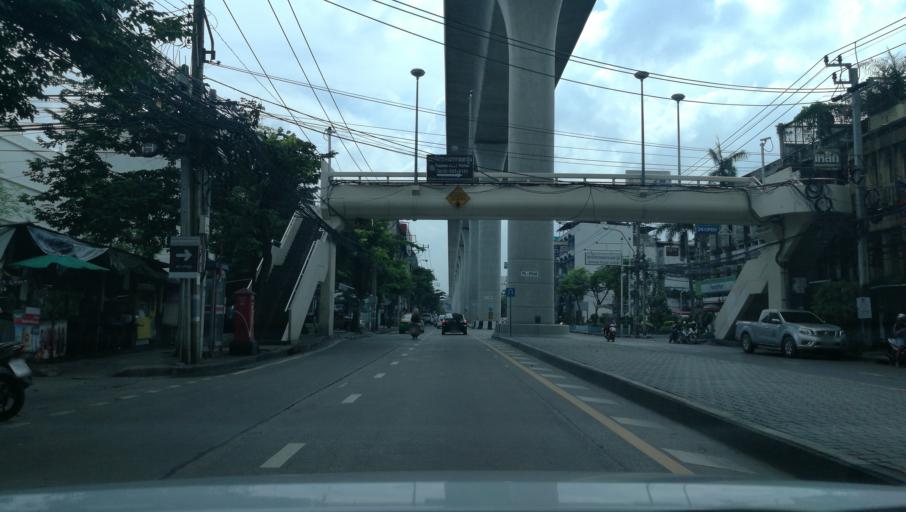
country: TH
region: Bangkok
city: Bang Sue
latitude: 13.8152
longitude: 100.5319
